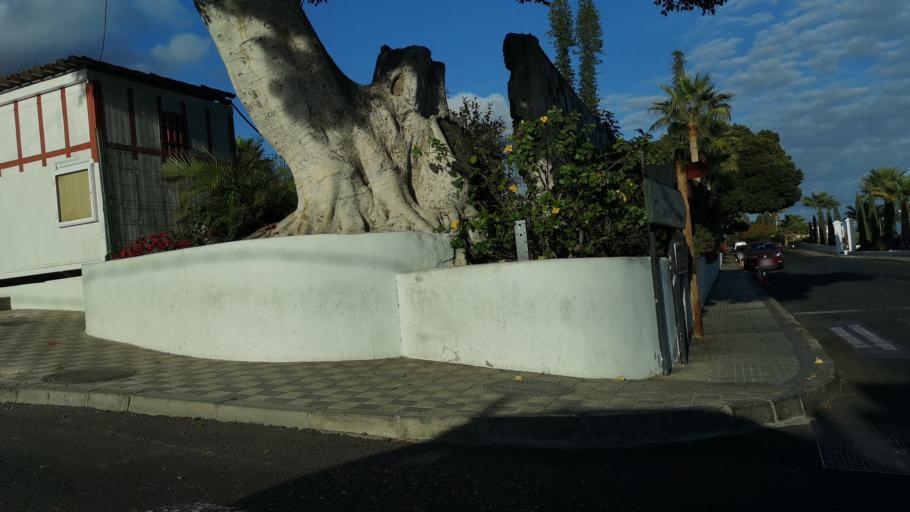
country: ES
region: Canary Islands
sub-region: Provincia de Santa Cruz de Tenerife
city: Alajero
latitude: 28.0312
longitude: -17.1903
